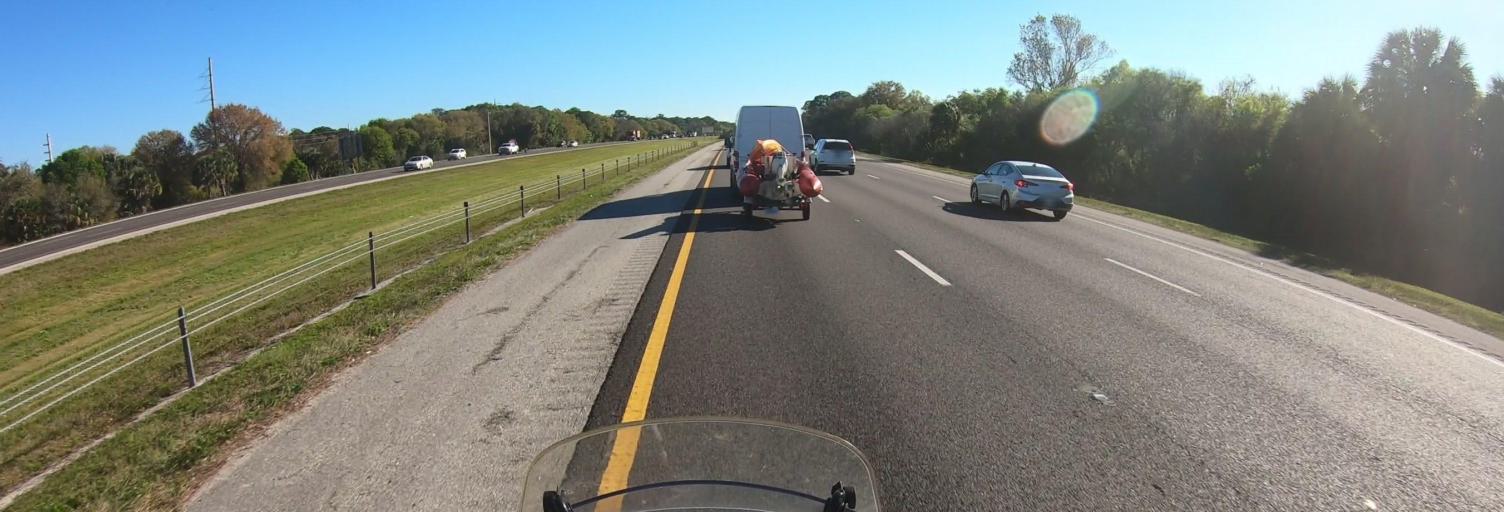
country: US
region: Florida
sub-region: Sarasota County
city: Lake Sarasota
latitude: 27.2509
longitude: -82.4509
